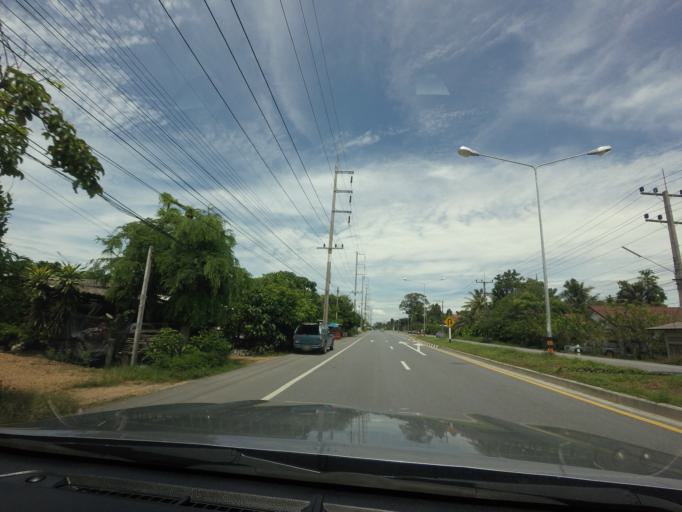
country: TH
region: Songkhla
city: Krasae Sin
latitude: 7.6146
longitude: 100.3975
